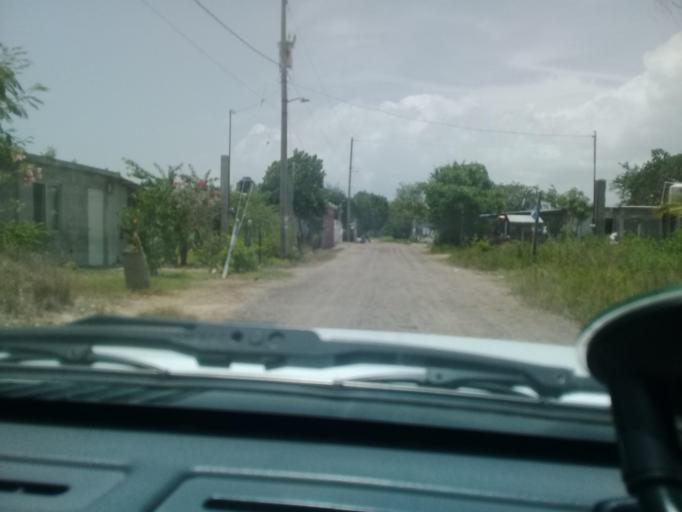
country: MX
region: Tamaulipas
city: Ciudad Madero
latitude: 22.2319
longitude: -97.8172
